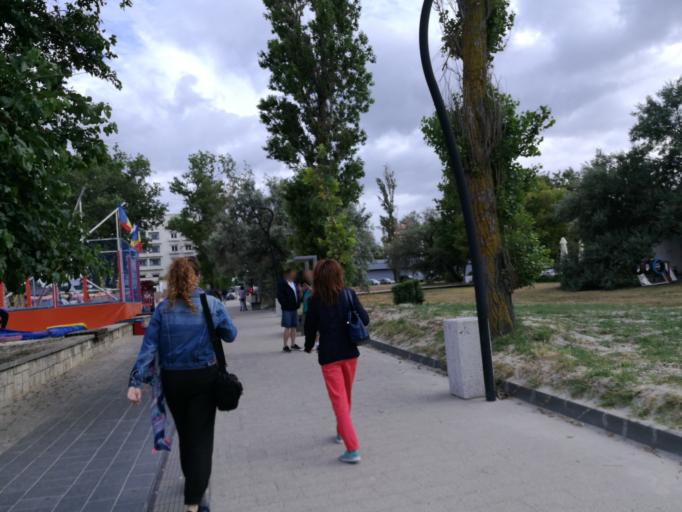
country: RO
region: Constanta
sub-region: Municipiul Constanta
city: Palazu Mare
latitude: 44.2497
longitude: 28.6219
